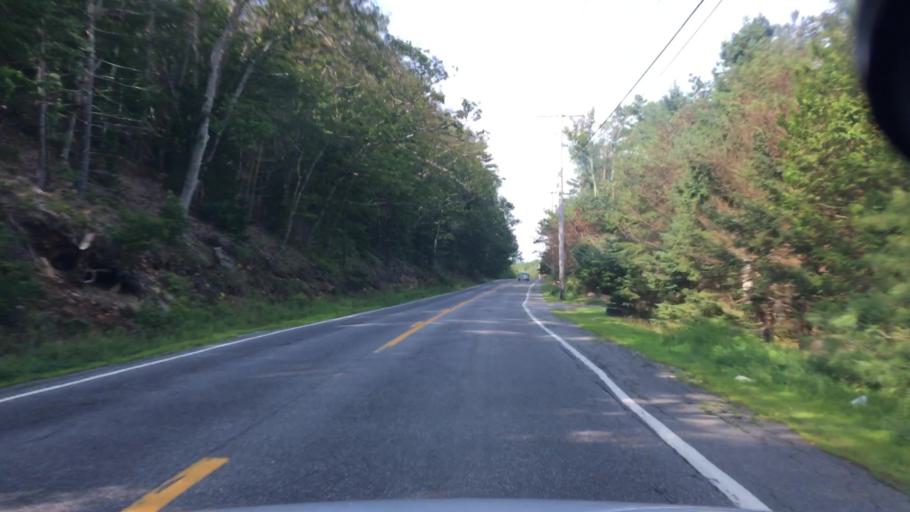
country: US
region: Maine
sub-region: Cumberland County
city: Harpswell Center
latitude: 43.8010
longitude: -69.9338
